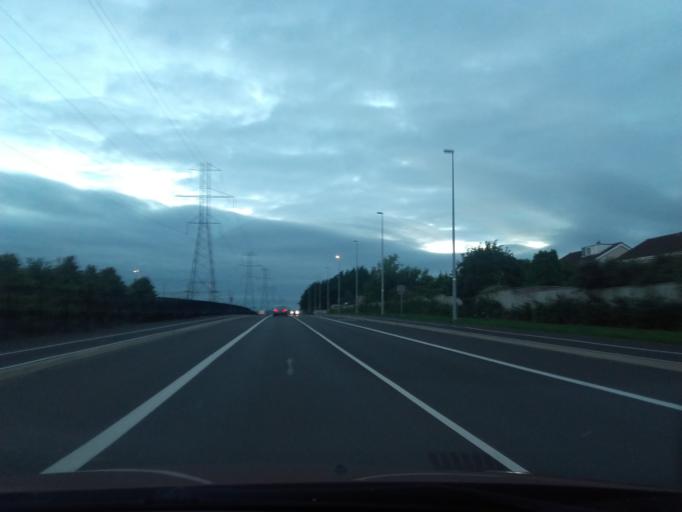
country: IE
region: Leinster
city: Tallaght
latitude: 53.2970
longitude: -6.3814
